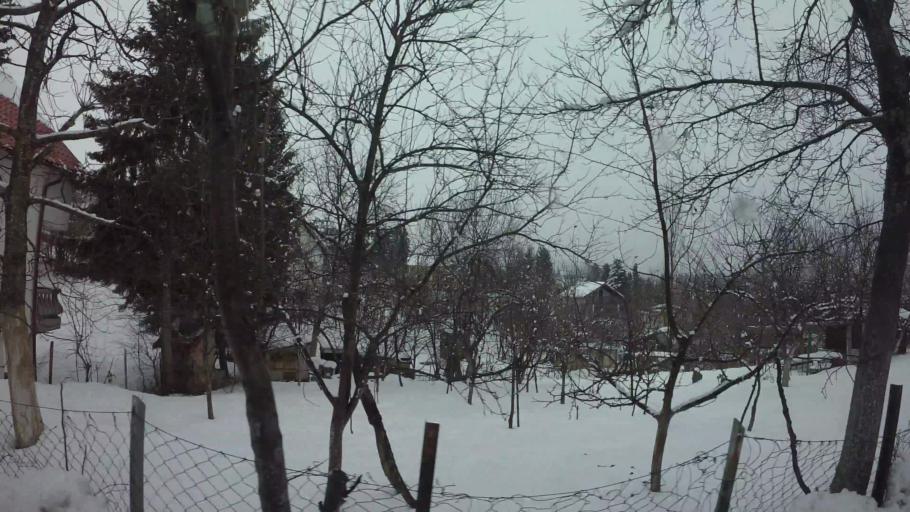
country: BA
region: Federation of Bosnia and Herzegovina
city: Hadzici
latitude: 43.8596
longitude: 18.2610
